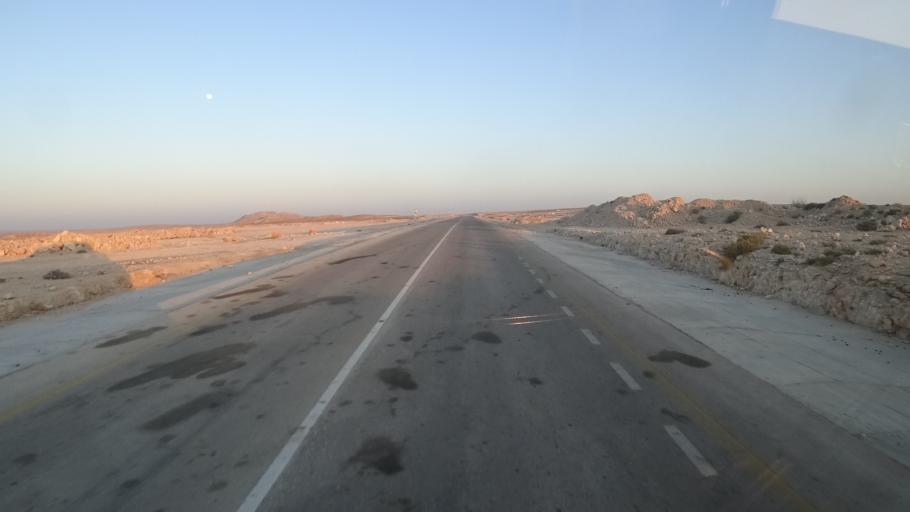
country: YE
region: Al Mahrah
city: Hawf
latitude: 16.9517
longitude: 53.3457
